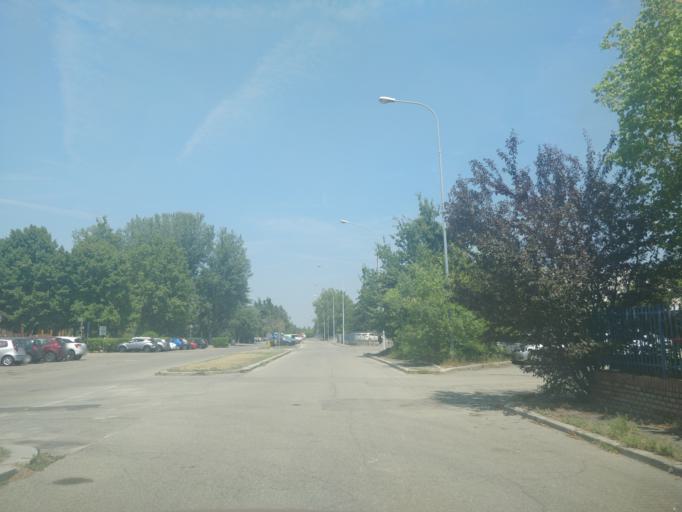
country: IT
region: Emilia-Romagna
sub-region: Provincia di Bologna
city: Progresso
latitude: 44.5604
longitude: 11.3707
